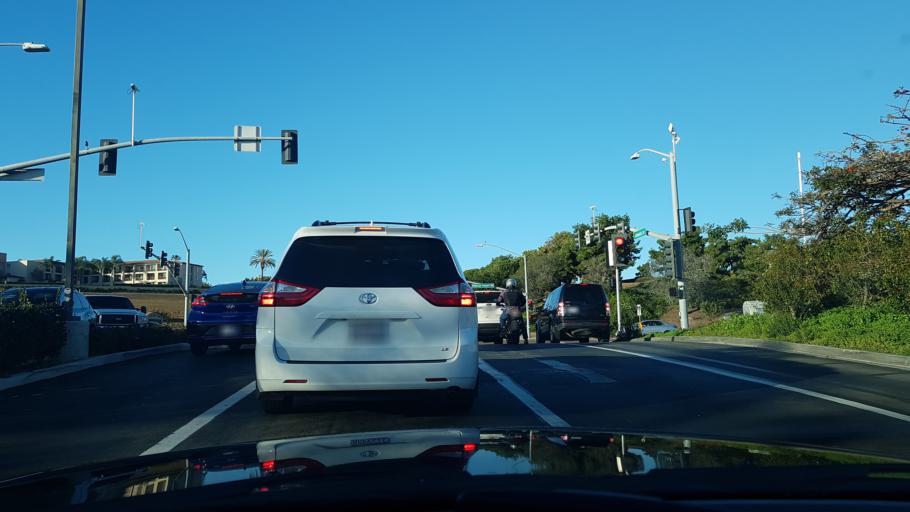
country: US
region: California
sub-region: San Diego County
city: Carlsbad
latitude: 33.1215
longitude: -117.3135
